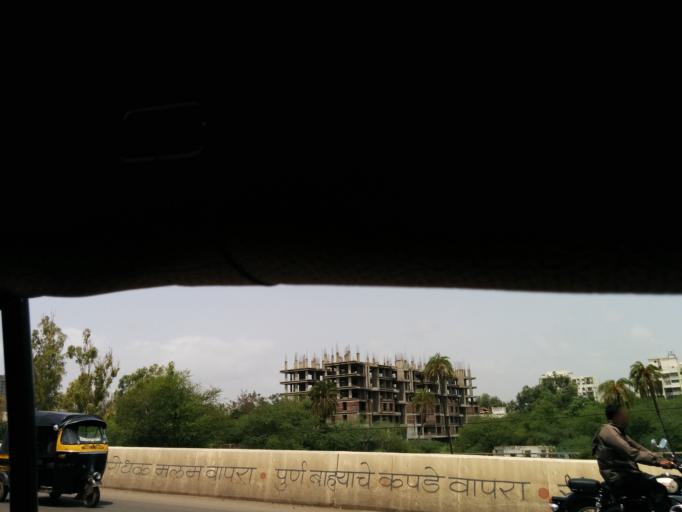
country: IN
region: Maharashtra
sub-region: Pune Division
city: Lohogaon
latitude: 18.5282
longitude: 73.9323
